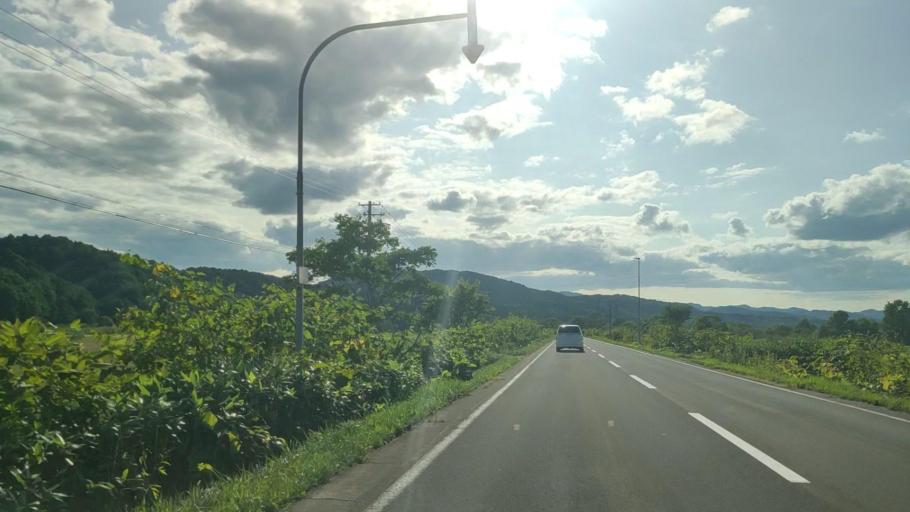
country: JP
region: Hokkaido
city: Nayoro
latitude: 44.7299
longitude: 142.0803
